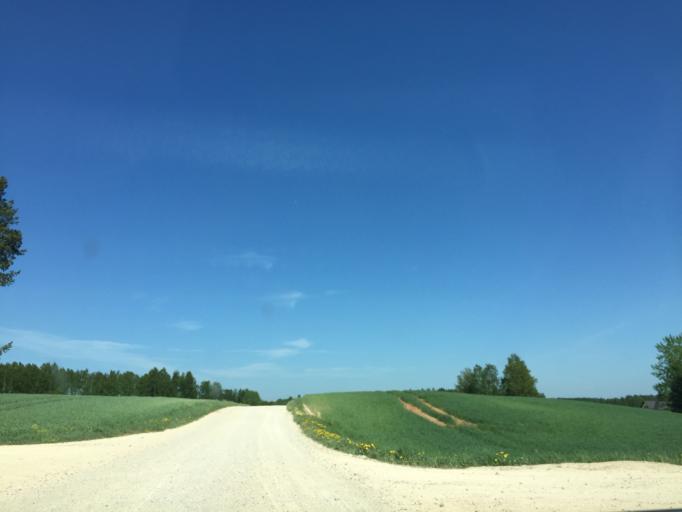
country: LV
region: Ikskile
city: Ikskile
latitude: 56.8660
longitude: 24.5020
